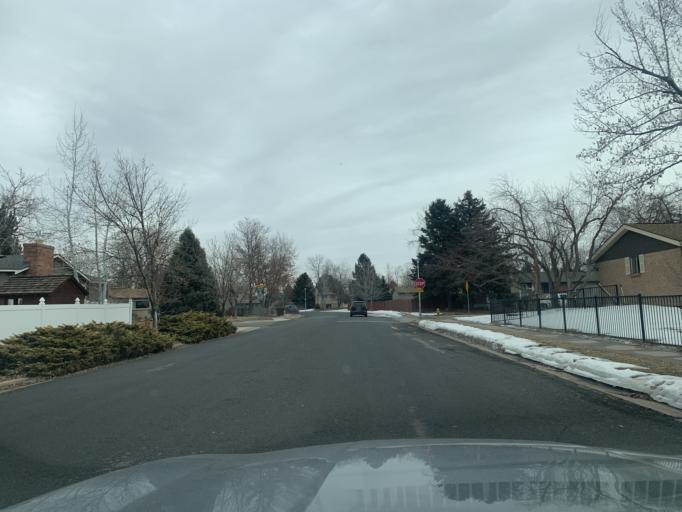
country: US
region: Colorado
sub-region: Arapahoe County
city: Glendale
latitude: 39.6613
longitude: -104.8756
